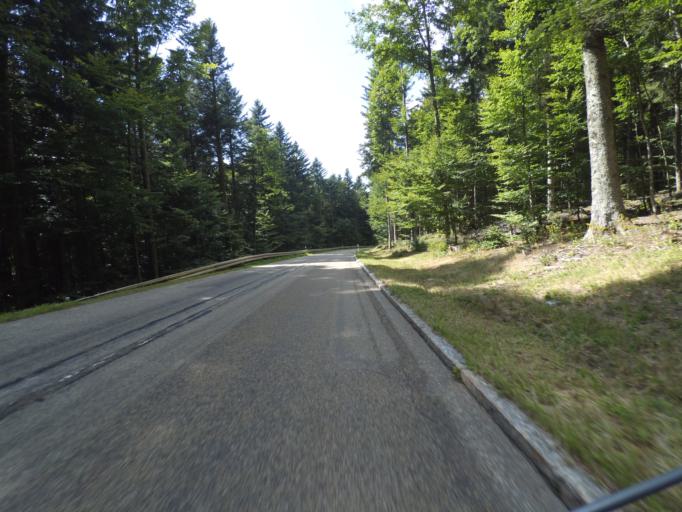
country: DE
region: Baden-Wuerttemberg
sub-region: Freiburg Region
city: Sankt Peter
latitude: 48.0488
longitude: 8.0489
